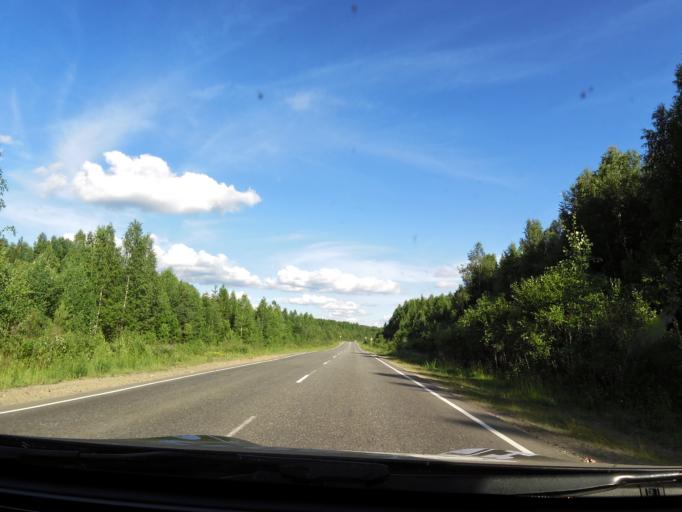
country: RU
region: Kirov
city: Omutninsk
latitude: 58.7525
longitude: 52.0505
